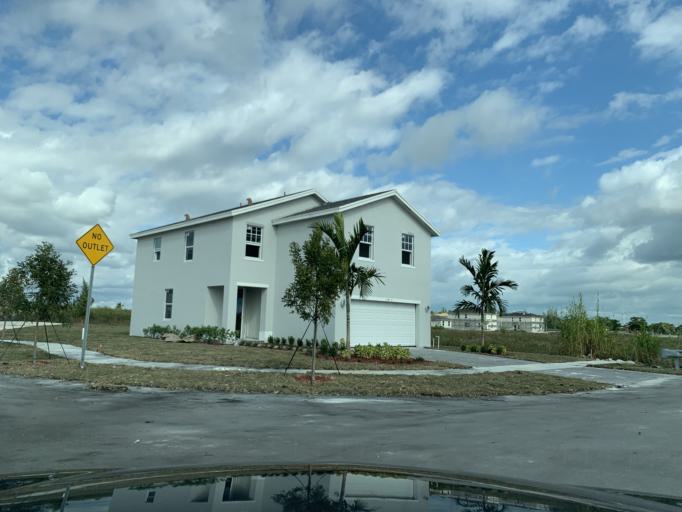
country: US
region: Florida
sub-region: Miami-Dade County
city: Naranja
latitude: 25.5125
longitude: -80.4086
